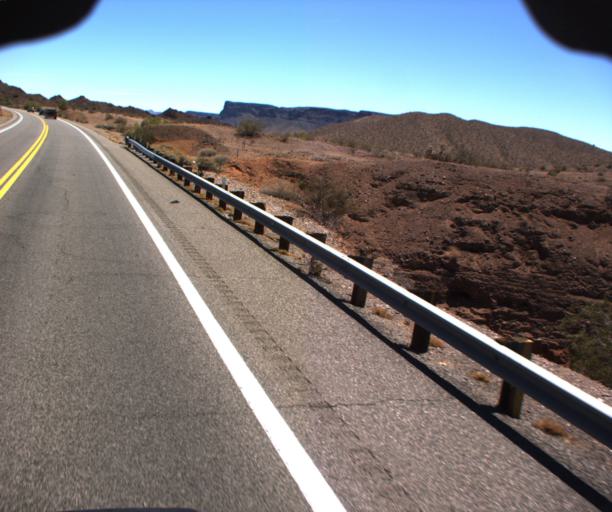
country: US
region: Arizona
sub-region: La Paz County
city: Cienega Springs
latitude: 34.3259
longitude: -114.1293
